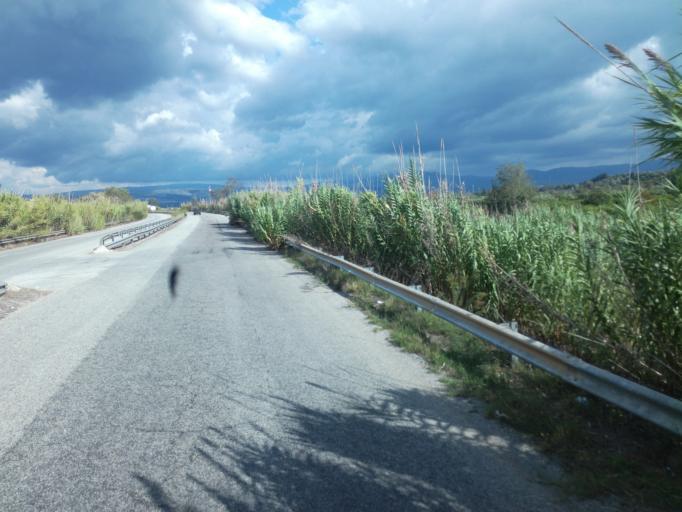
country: IT
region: Calabria
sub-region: Provincia di Reggio Calabria
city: Rosarno
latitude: 38.4762
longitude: 15.9834
